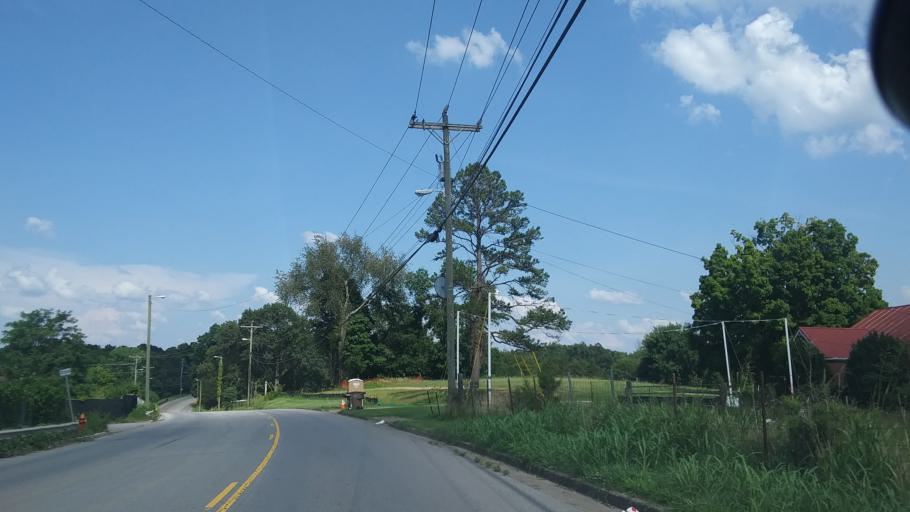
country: US
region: Tennessee
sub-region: Rutherford County
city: La Vergne
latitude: 36.0964
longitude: -86.6494
